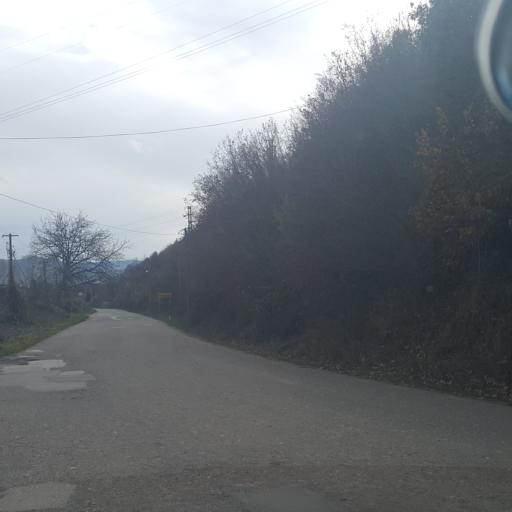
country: RS
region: Central Serbia
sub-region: Zajecarski Okrug
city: Knjazevac
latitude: 43.5815
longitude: 22.2476
